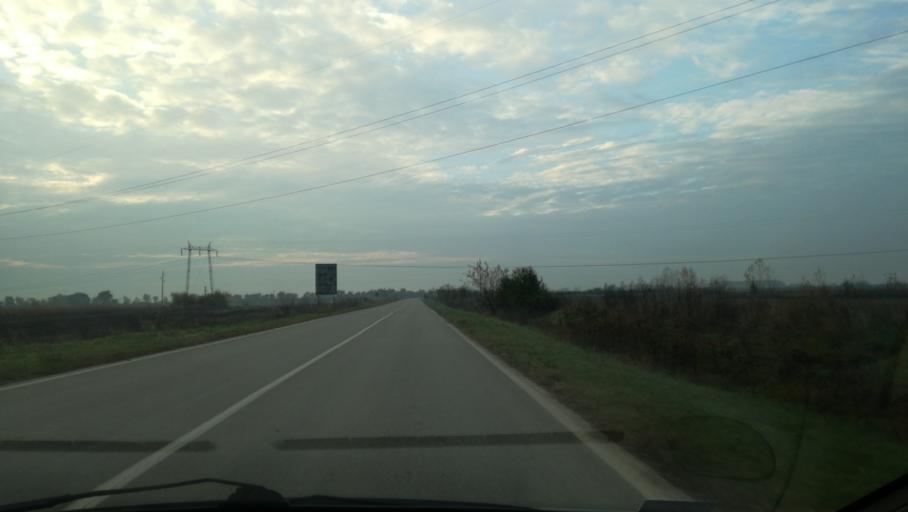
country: RS
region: Autonomna Pokrajina Vojvodina
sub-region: Severnobanatski Okrug
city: Kikinda
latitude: 45.8053
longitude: 20.4353
